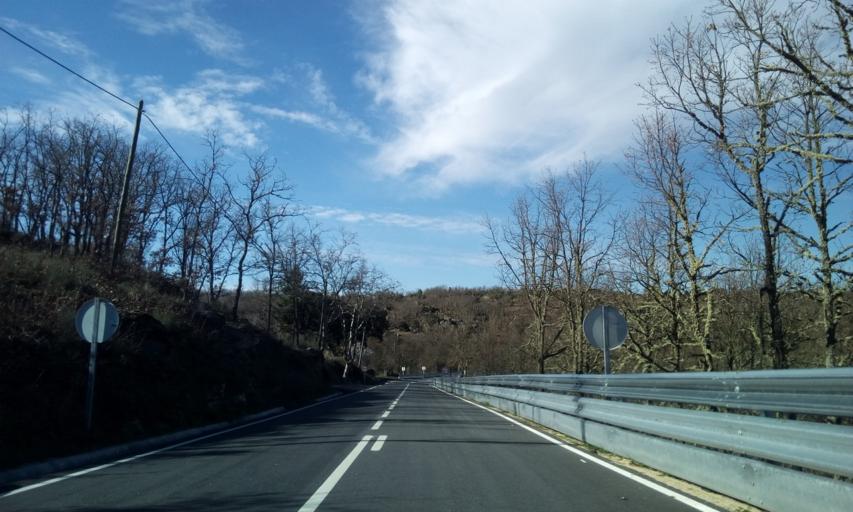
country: ES
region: Castille and Leon
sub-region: Provincia de Salamanca
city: Fuentes de Onoro
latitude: 40.5995
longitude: -6.9321
